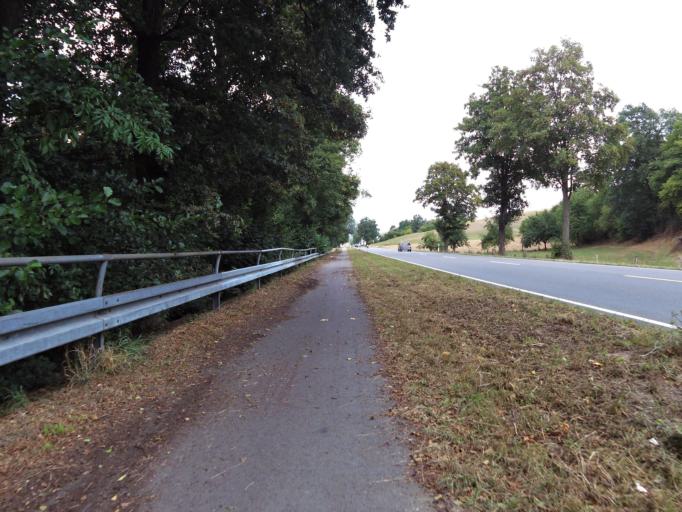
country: DE
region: Hesse
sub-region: Regierungsbezirk Darmstadt
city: Frankisch-Crumbach
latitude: 49.7426
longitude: 8.8743
